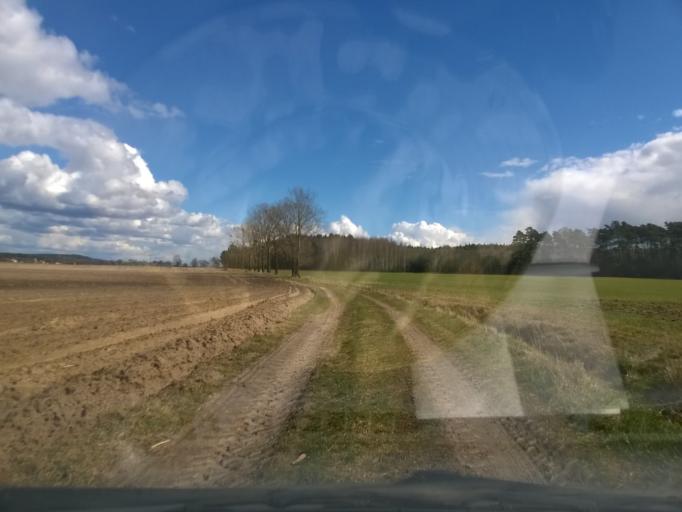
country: PL
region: Kujawsko-Pomorskie
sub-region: Powiat nakielski
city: Kcynia
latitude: 53.0332
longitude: 17.4068
